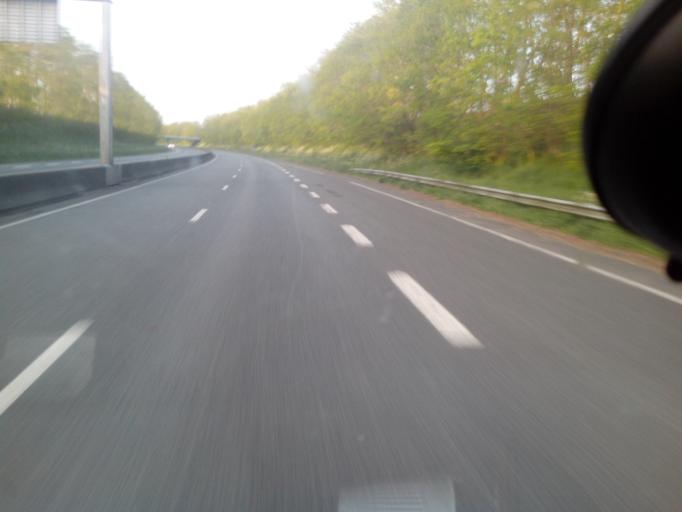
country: FR
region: Picardie
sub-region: Departement de la Somme
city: Abbeville
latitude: 50.0574
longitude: 1.7844
